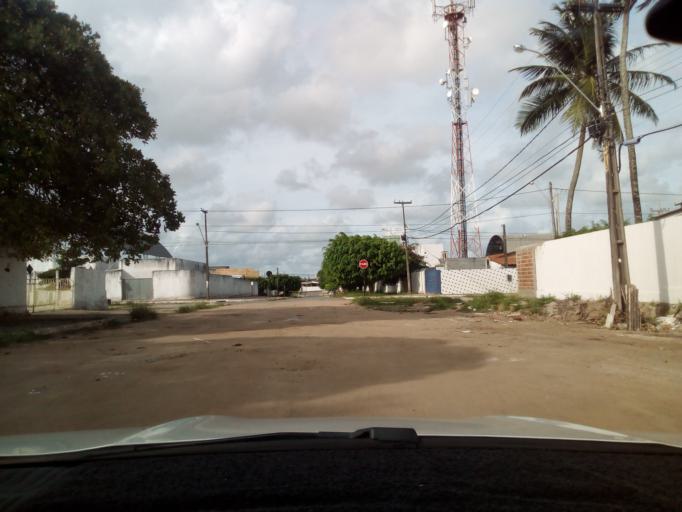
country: BR
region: Paraiba
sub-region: Joao Pessoa
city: Joao Pessoa
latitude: -7.1538
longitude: -34.8784
